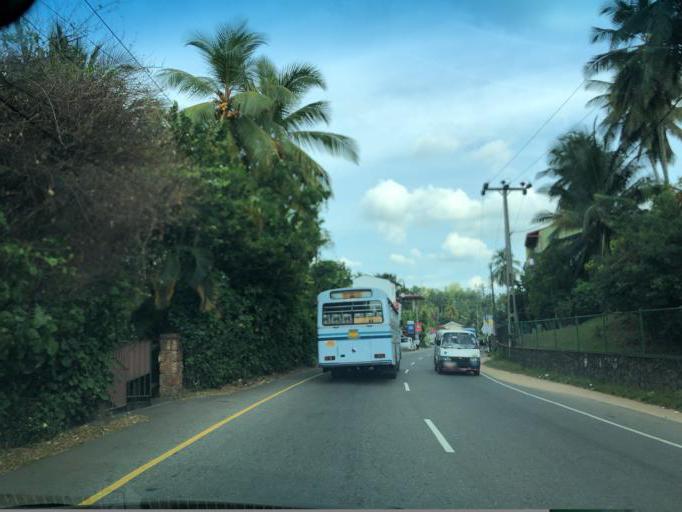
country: LK
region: Western
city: Horawala Junction
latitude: 6.5232
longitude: 80.1092
